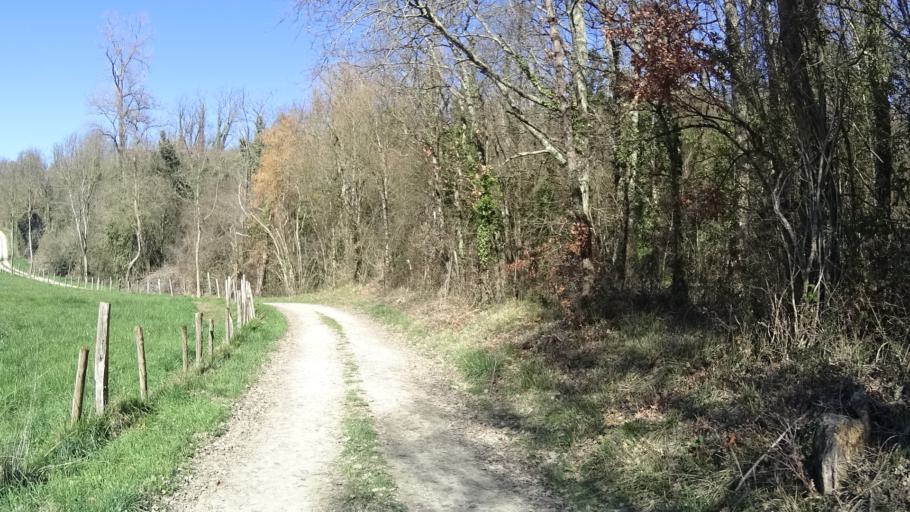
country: FR
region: Aquitaine
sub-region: Departement de la Dordogne
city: Riberac
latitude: 45.2129
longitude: 0.3297
